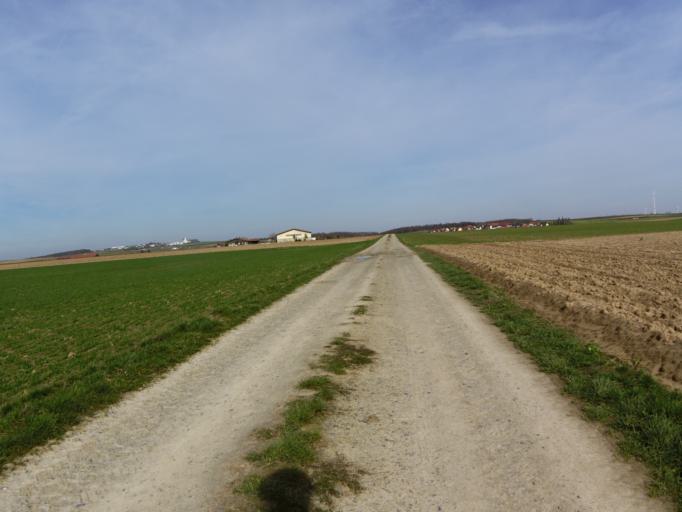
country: DE
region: Bavaria
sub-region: Regierungsbezirk Unterfranken
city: Biebelried
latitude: 49.7541
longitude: 10.0816
